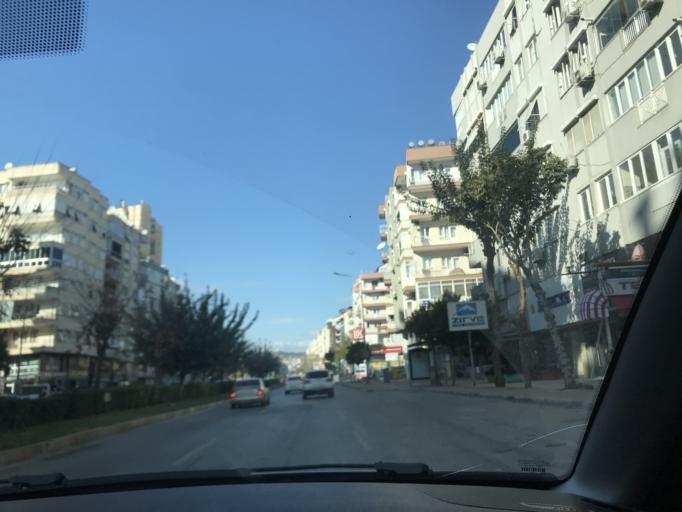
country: TR
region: Antalya
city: Antalya
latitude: 36.9055
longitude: 30.7003
